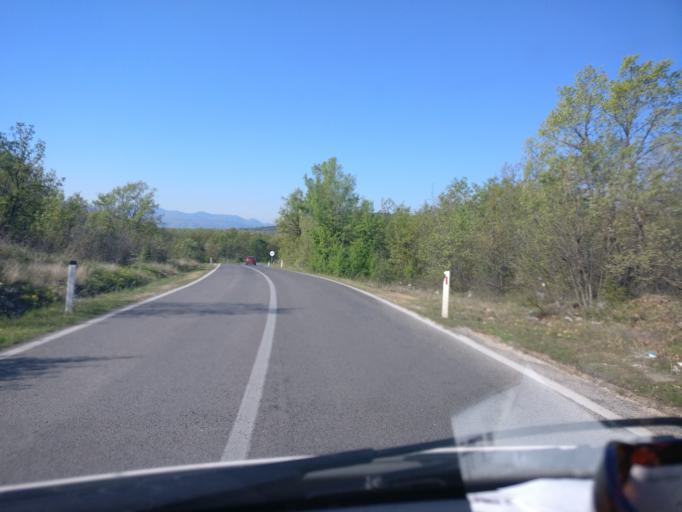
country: BA
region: Federation of Bosnia and Herzegovina
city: Tasovcici
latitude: 43.1293
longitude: 17.7652
